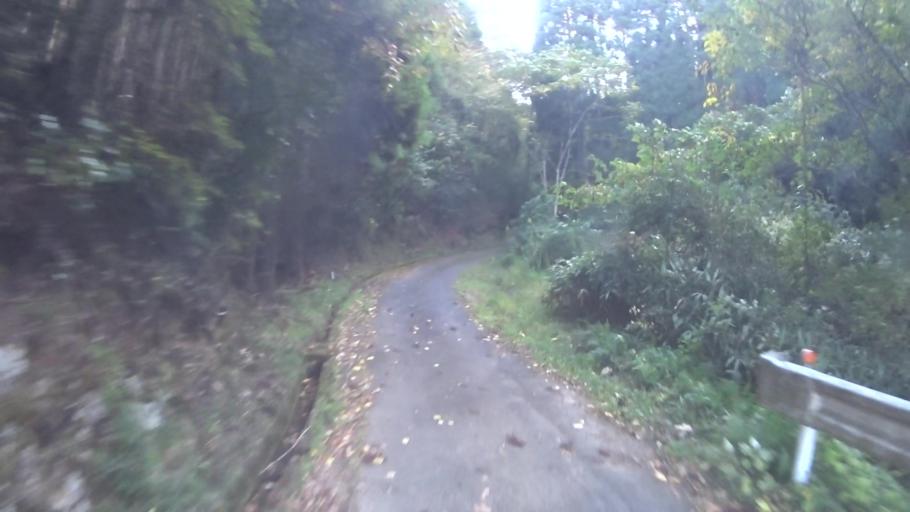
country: JP
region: Kyoto
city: Ayabe
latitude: 35.2716
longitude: 135.2488
